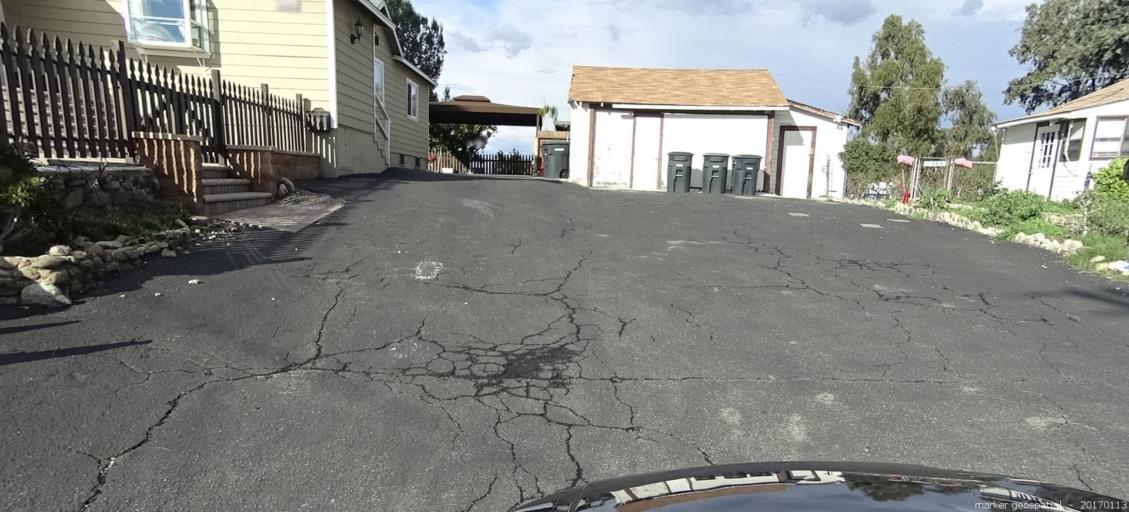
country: US
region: California
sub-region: Orange County
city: Villa Park
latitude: 33.8380
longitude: -117.8388
